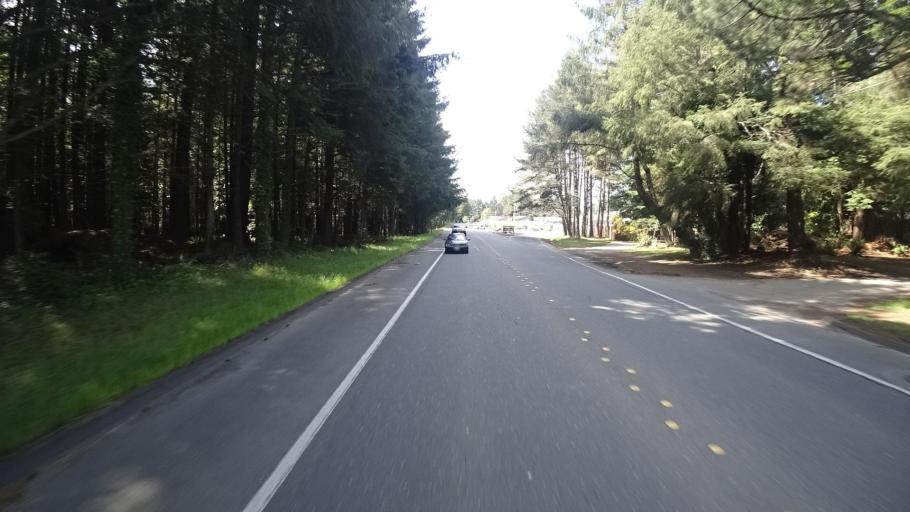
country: US
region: California
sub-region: Humboldt County
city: Cutten
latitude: 40.7594
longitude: -124.1457
